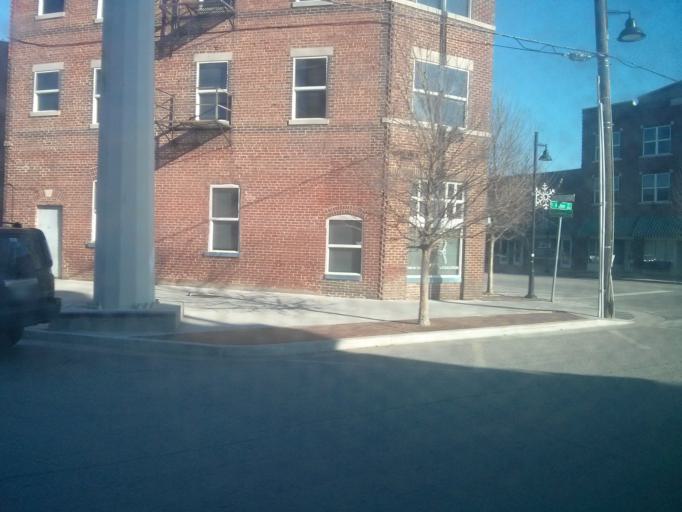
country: US
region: Oklahoma
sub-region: Tulsa County
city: Tulsa
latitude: 36.1597
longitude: -95.9863
